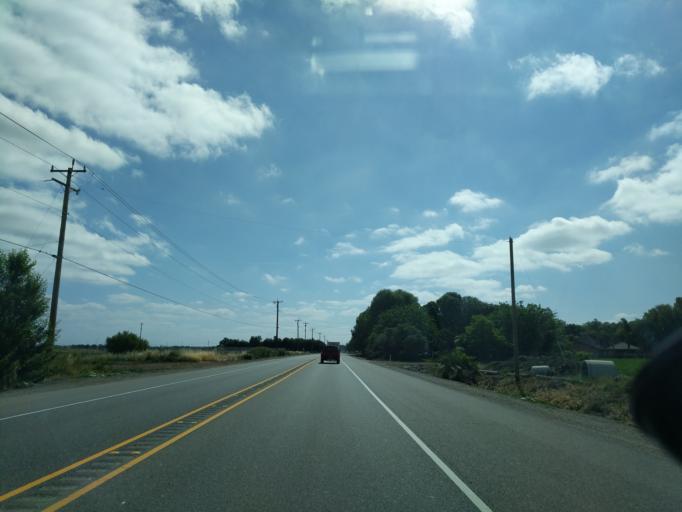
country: US
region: California
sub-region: Contra Costa County
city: Byron
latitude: 37.8965
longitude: -121.6532
